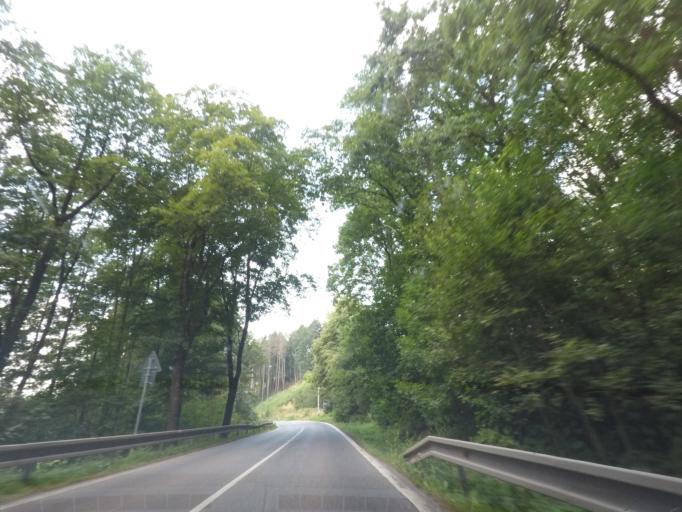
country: CZ
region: Kralovehradecky
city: Pilnikov
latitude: 50.5498
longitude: 15.8412
